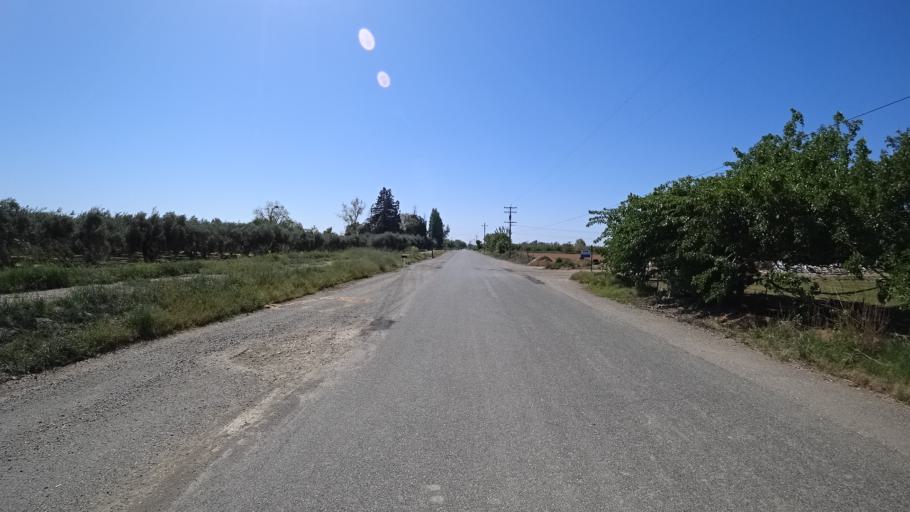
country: US
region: California
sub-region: Glenn County
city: Orland
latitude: 39.7745
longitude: -122.1597
